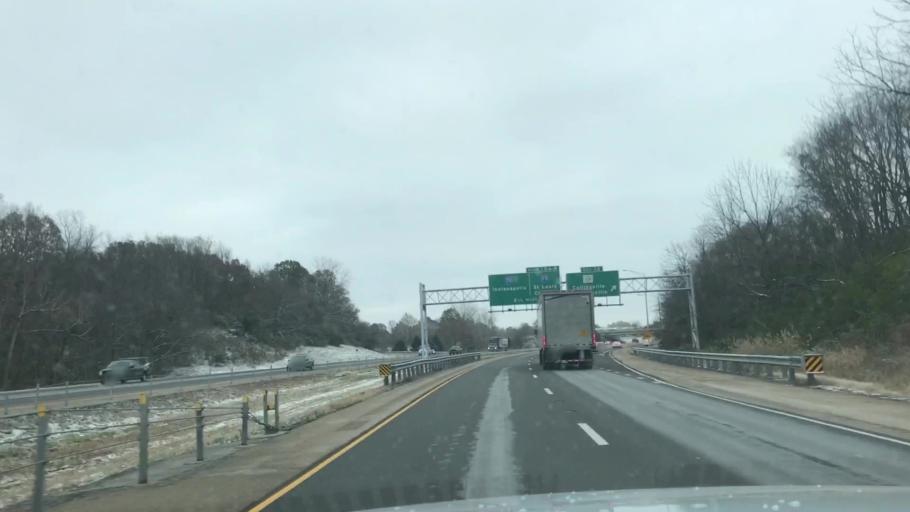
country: US
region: Illinois
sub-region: Madison County
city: Glen Carbon
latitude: 38.7567
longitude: -89.9623
